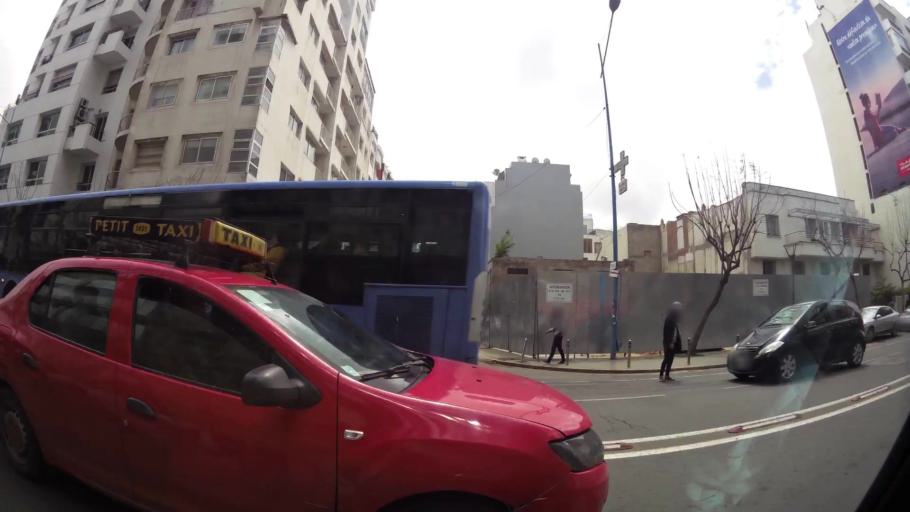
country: MA
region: Grand Casablanca
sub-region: Casablanca
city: Casablanca
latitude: 33.5918
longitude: -7.6343
